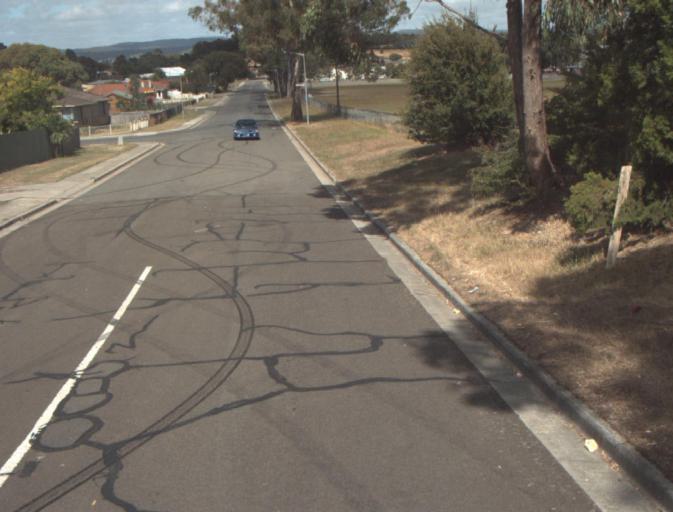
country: AU
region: Tasmania
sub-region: Launceston
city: Newstead
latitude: -41.4156
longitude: 147.1811
